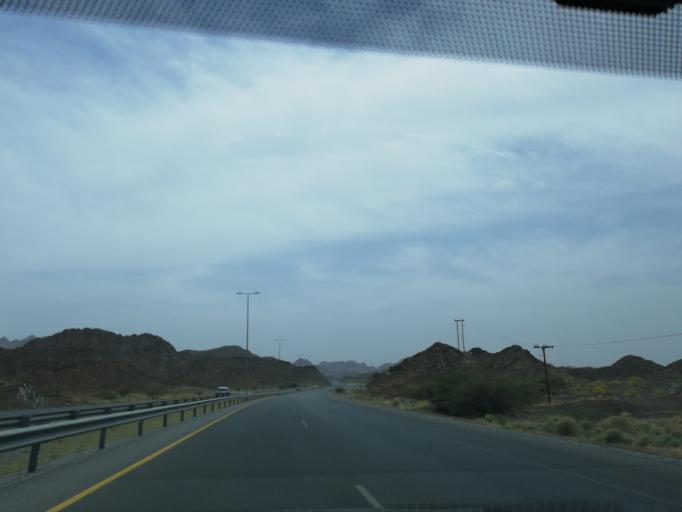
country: OM
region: Muhafazat ad Dakhiliyah
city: Izki
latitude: 22.9466
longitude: 57.7895
